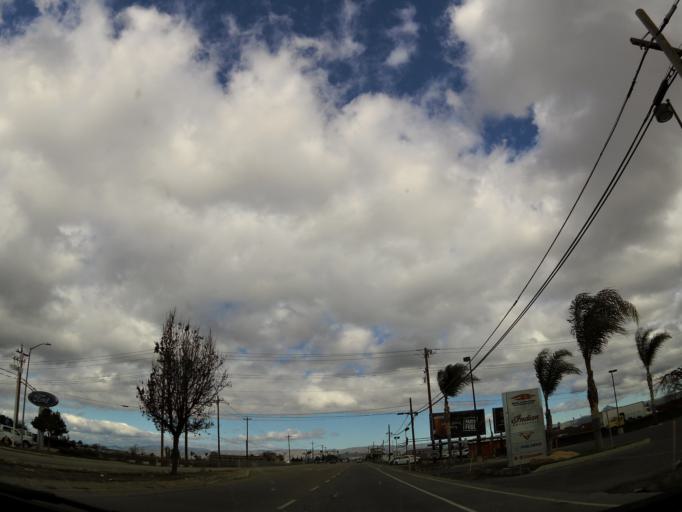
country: US
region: California
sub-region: San Benito County
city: Hollister
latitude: 36.8625
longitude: -121.4014
